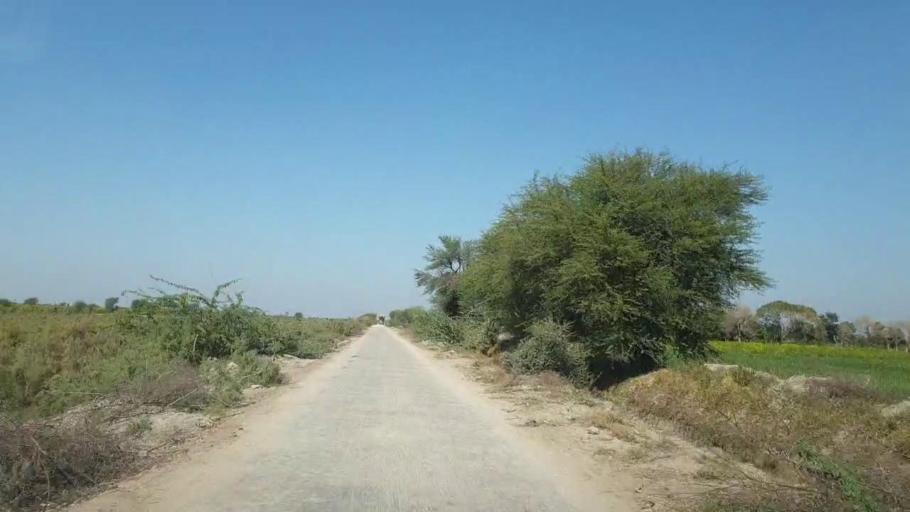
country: PK
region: Sindh
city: Mirpur Khas
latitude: 25.6593
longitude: 69.0270
